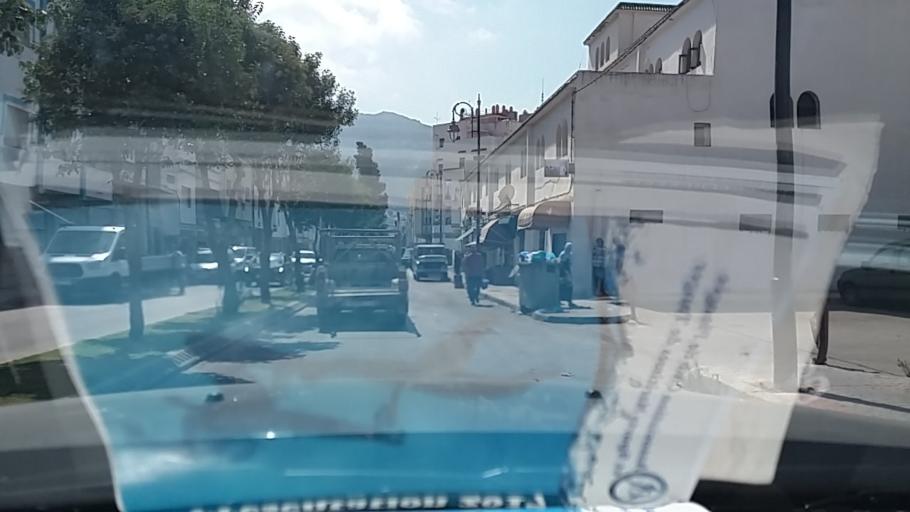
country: MA
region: Tanger-Tetouan
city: Tetouan
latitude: 35.5648
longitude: -5.3587
